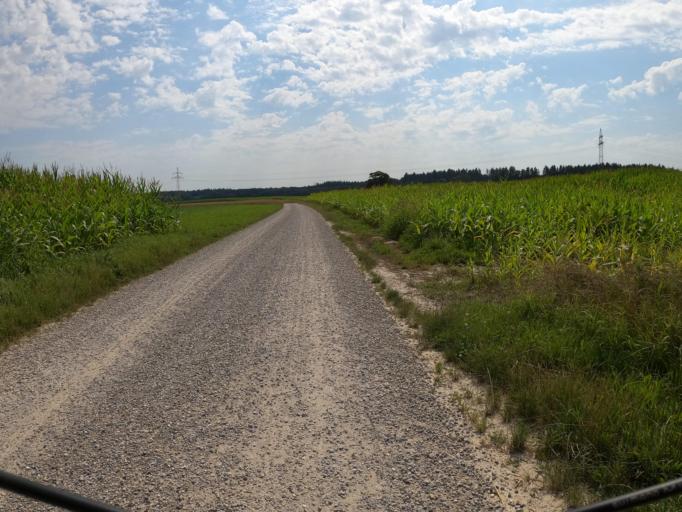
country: DE
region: Bavaria
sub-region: Swabia
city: Rieden an der Kotz
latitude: 48.3778
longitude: 10.2201
